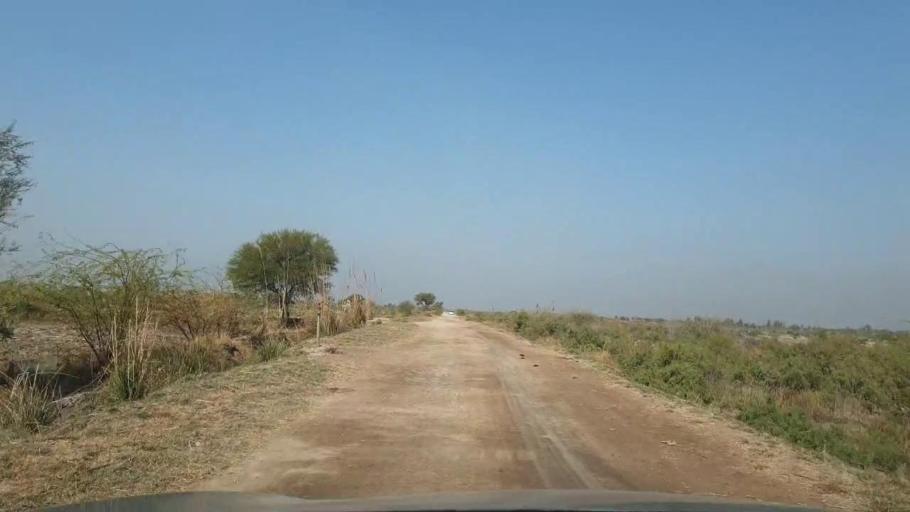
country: PK
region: Sindh
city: Berani
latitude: 25.7124
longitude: 68.8595
